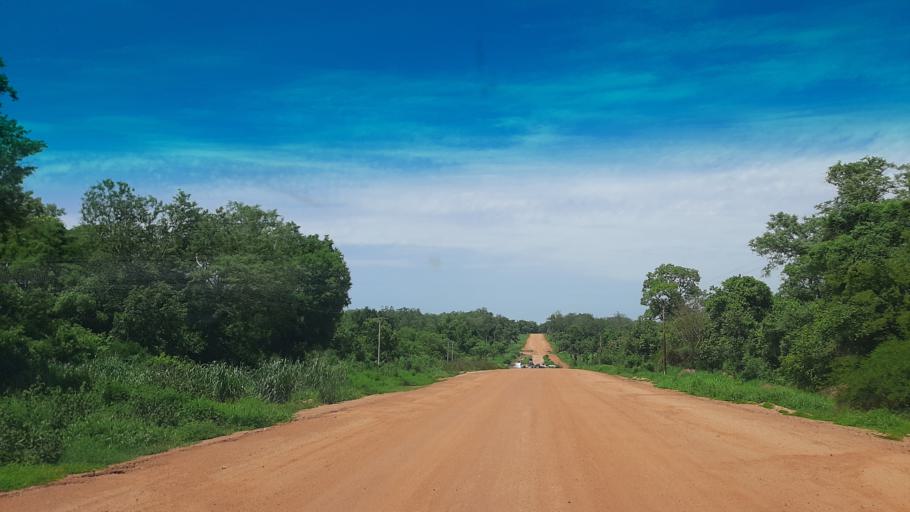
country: ET
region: Gambela
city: Gambela
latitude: 8.0910
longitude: 34.5892
